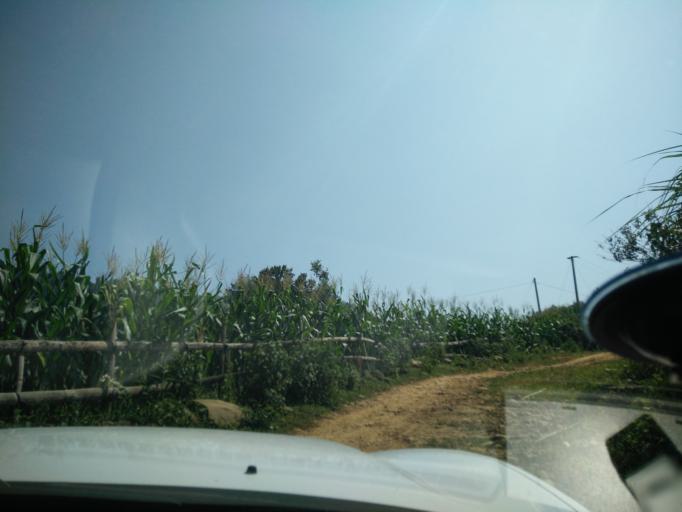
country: CN
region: Guangxi Zhuangzu Zizhiqu
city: Xinzhou
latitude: 25.1846
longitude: 105.6940
